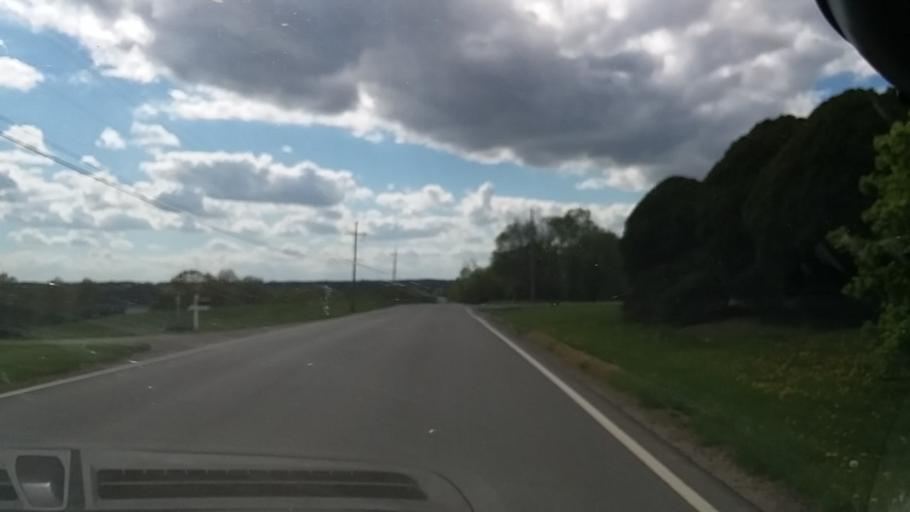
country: US
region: Kansas
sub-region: Douglas County
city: Lawrence
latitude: 38.8991
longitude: -95.2468
